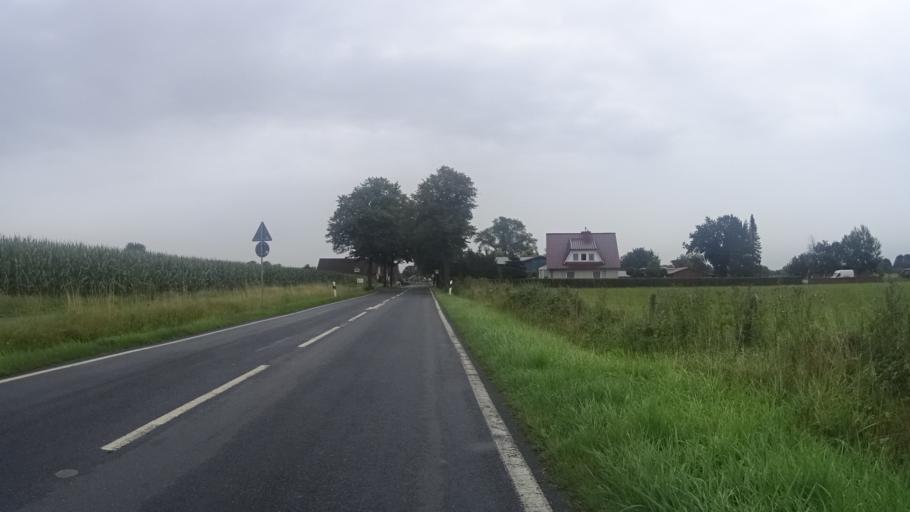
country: DE
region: Schleswig-Holstein
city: Bevern
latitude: 53.7568
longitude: 9.7589
